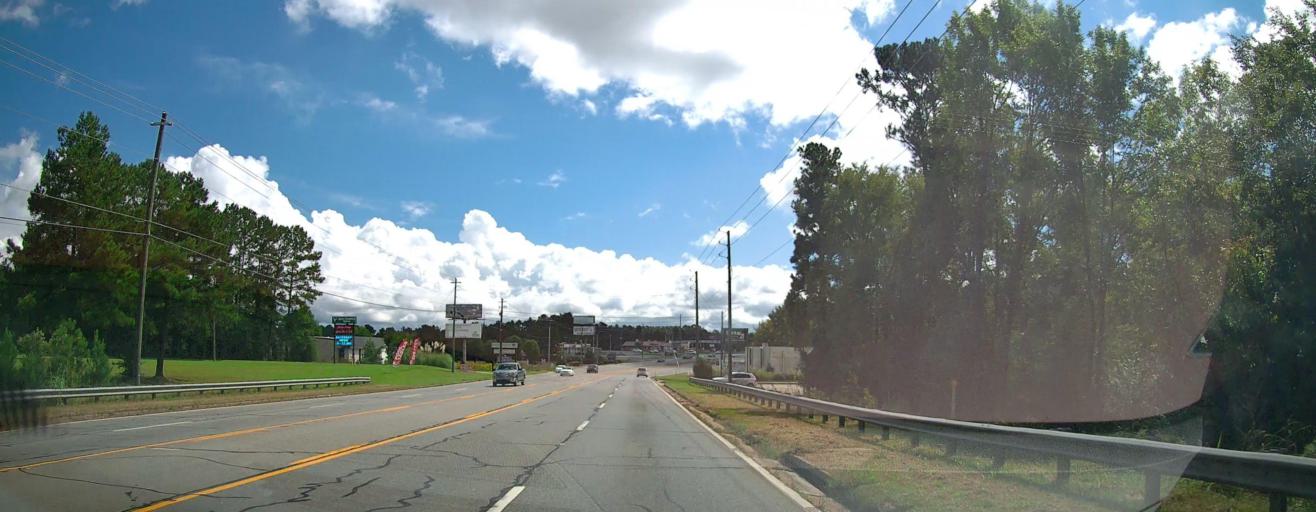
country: US
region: Georgia
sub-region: Baldwin County
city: Milledgeville
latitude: 33.1003
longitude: -83.2601
